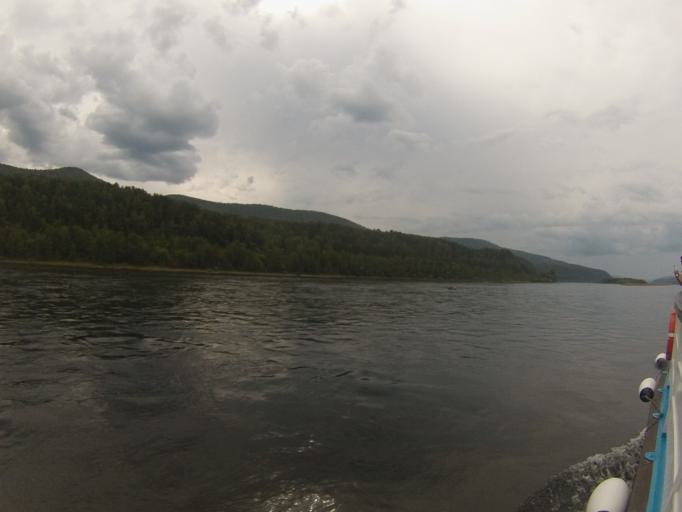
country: RU
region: Krasnoyarskiy
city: Ovsyanka
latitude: 55.9693
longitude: 92.7036
